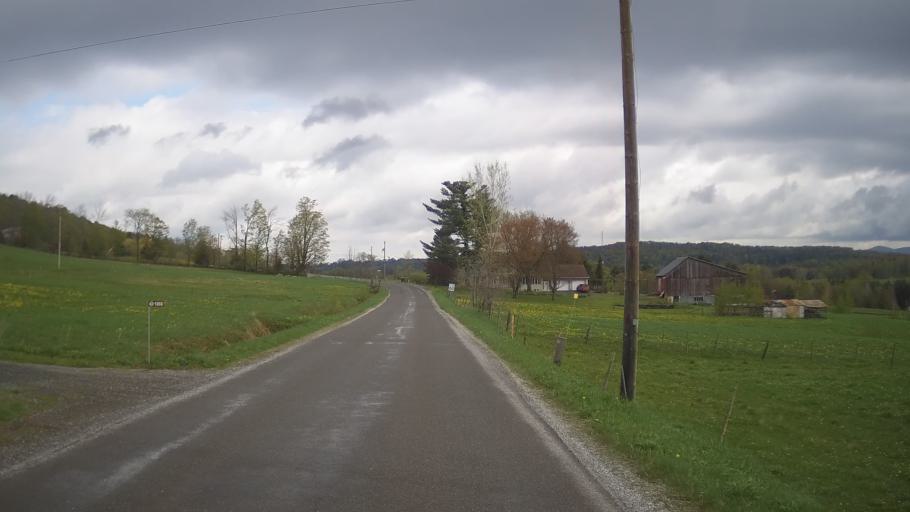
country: CA
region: Quebec
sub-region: Monteregie
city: Cowansville
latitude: 45.1878
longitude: -72.6981
